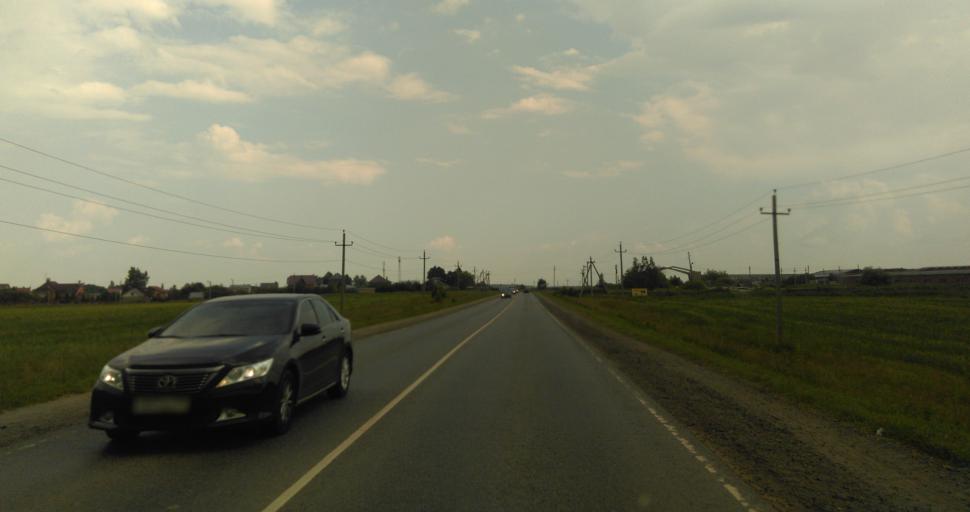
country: RU
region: Moskovskaya
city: Belyye Stolby
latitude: 55.3824
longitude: 37.8718
